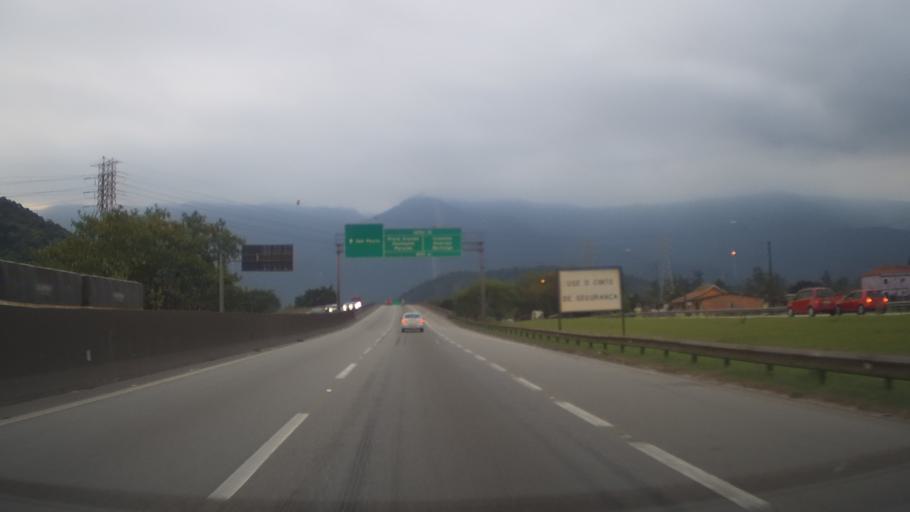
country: BR
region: Sao Paulo
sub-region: Cubatao
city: Cubatao
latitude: -23.8983
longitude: -46.4310
